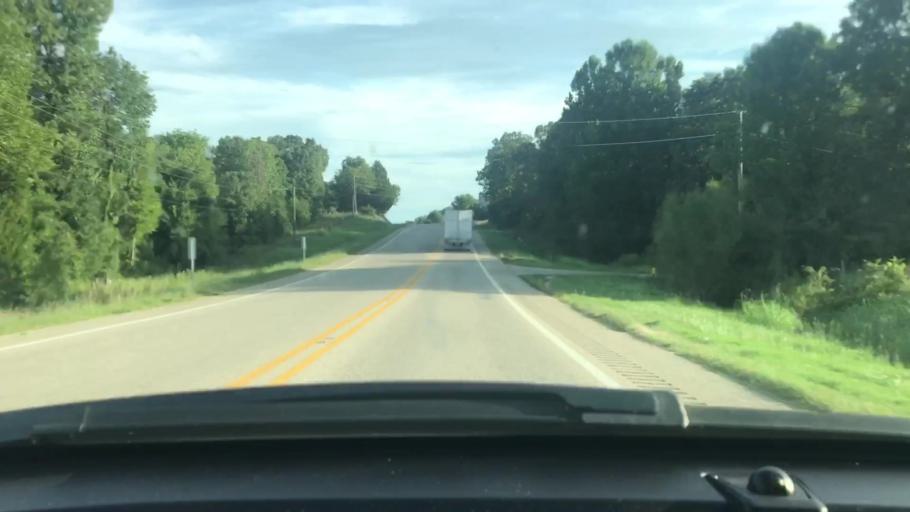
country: US
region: Arkansas
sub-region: Lawrence County
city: Hoxie
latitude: 36.1574
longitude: -91.1618
